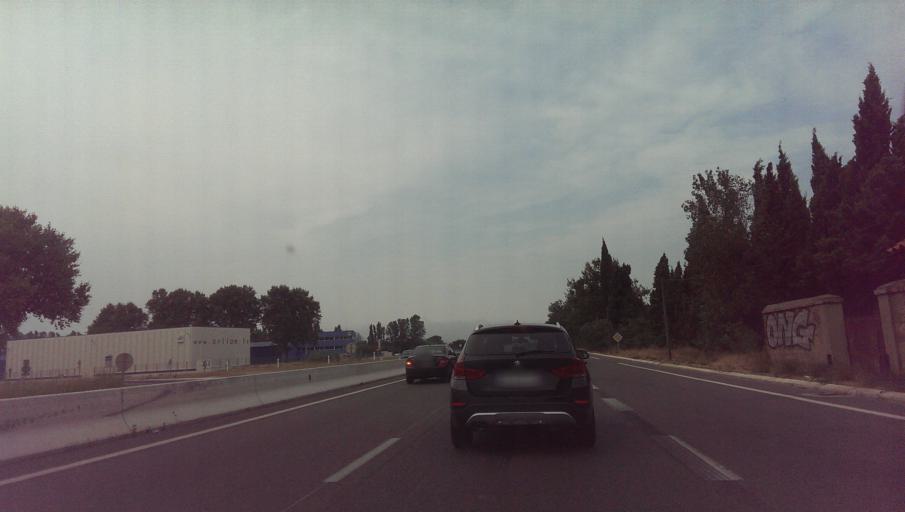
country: FR
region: Languedoc-Roussillon
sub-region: Departement des Pyrenees-Orientales
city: Rivesaltes
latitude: 42.7693
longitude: 2.9004
